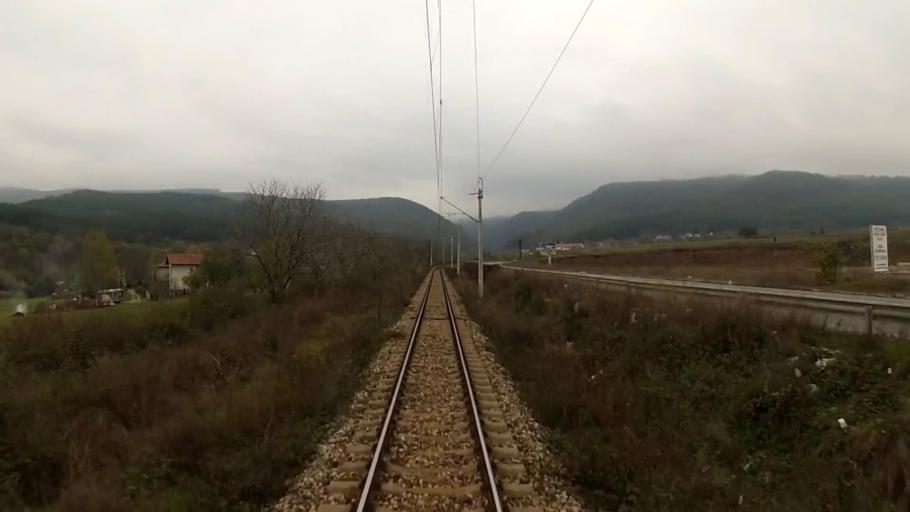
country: RS
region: Central Serbia
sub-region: Pirotski Okrug
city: Dimitrovgrad
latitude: 42.9832
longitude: 22.8503
